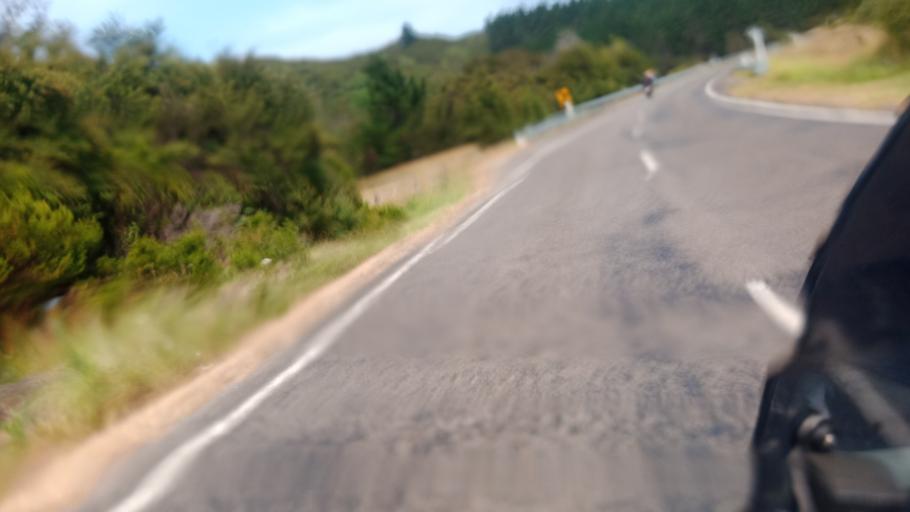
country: NZ
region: Bay of Plenty
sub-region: Opotiki District
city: Opotiki
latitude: -37.6051
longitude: 178.2651
